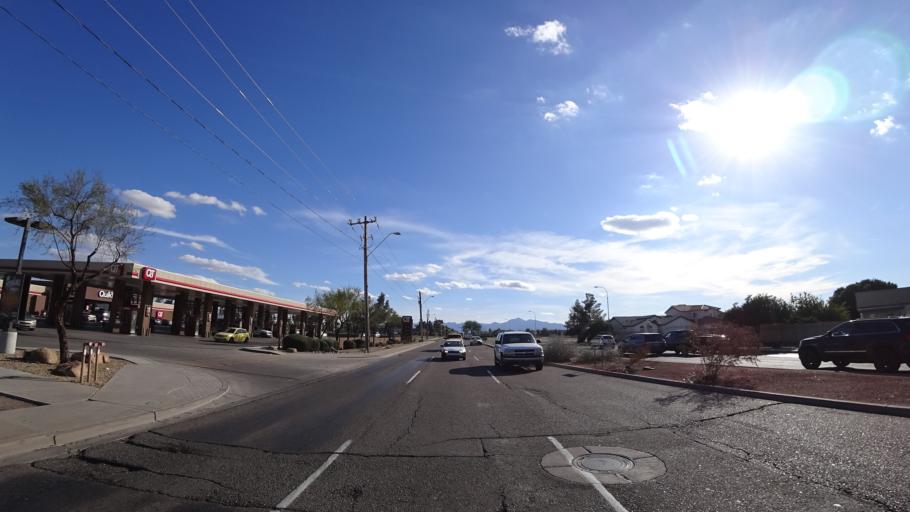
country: US
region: Arizona
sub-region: Maricopa County
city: Tolleson
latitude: 33.4718
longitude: -112.2378
